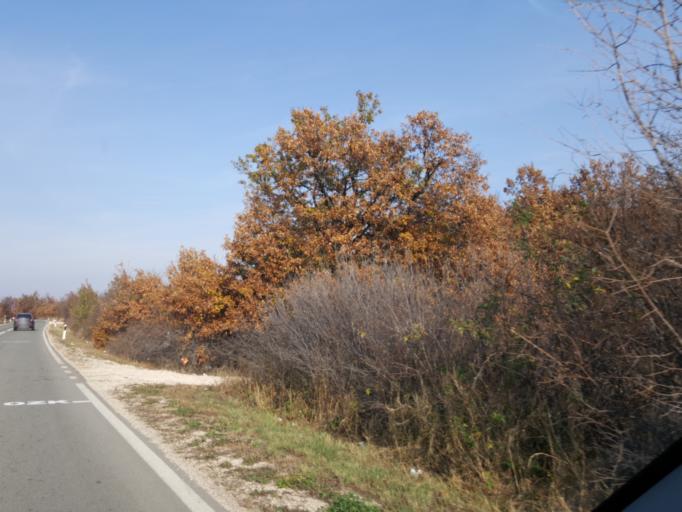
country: RS
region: Central Serbia
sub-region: Borski Okrug
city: Bor
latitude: 44.0074
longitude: 22.0717
